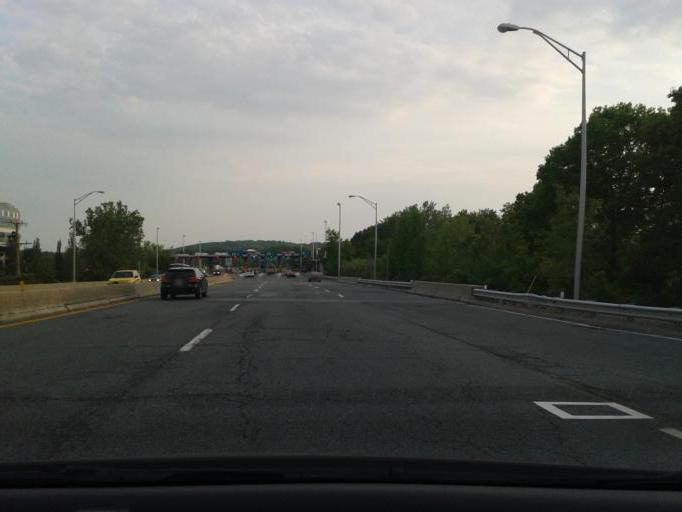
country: US
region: Massachusetts
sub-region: Middlesex County
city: Cochituate
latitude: 42.3118
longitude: -71.3856
